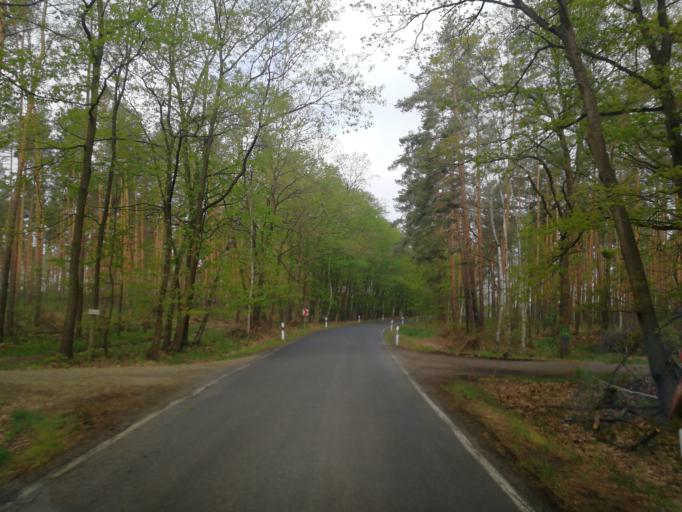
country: DE
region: Brandenburg
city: Herzberg
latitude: 51.6431
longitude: 13.1409
